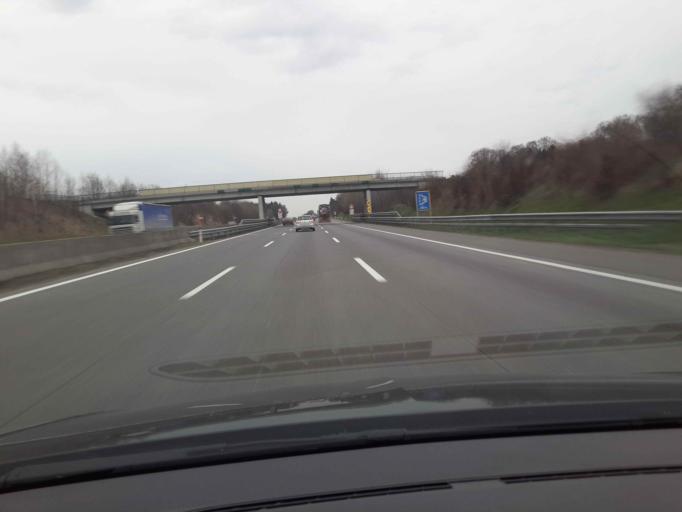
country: AT
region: Lower Austria
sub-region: Politischer Bezirk Melk
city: Blindenmarkt
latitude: 48.1369
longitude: 14.9719
